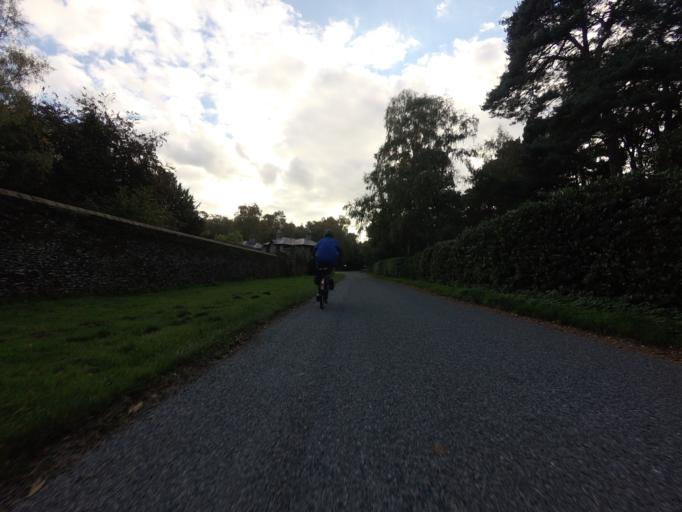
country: GB
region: England
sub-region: Norfolk
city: Dersingham
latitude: 52.8196
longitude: 0.4950
